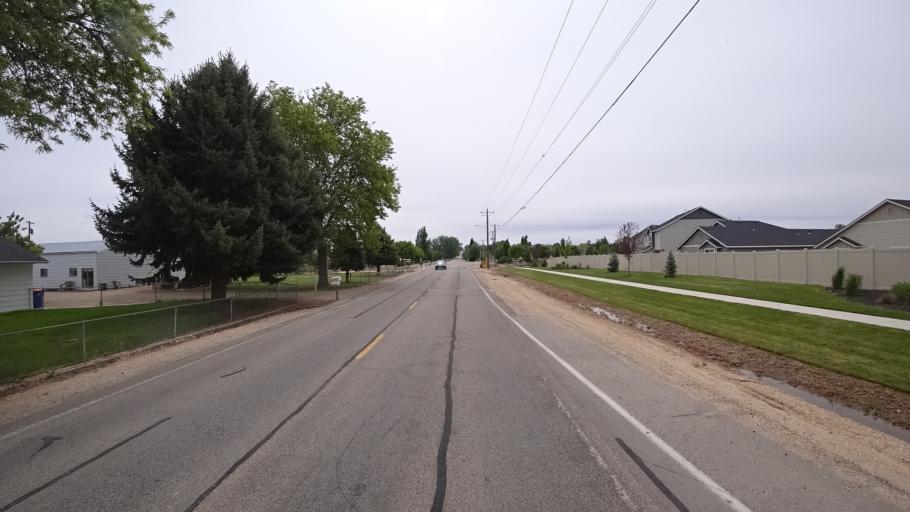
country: US
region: Idaho
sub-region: Ada County
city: Meridian
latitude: 43.5668
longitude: -116.3746
